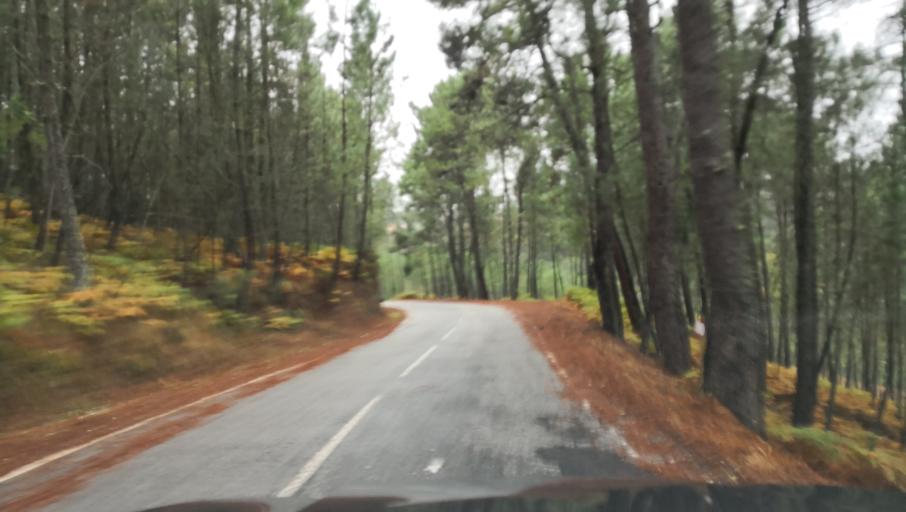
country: PT
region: Vila Real
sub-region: Sabrosa
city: Sabrosa
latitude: 41.3445
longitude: -7.5880
